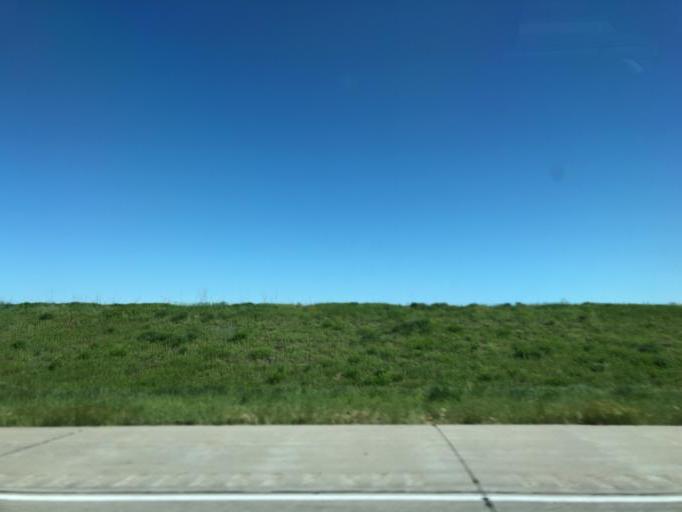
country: US
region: Nebraska
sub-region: Lancaster County
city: Waverly
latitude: 40.9086
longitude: -96.4967
